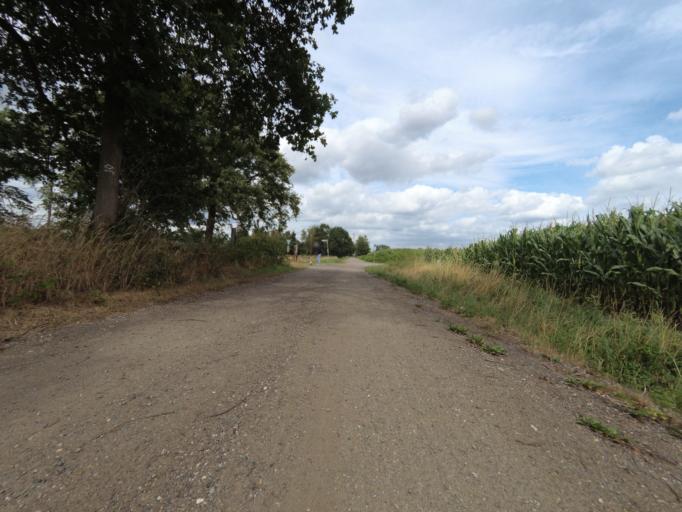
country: DE
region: North Rhine-Westphalia
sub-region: Regierungsbezirk Munster
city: Gronau
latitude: 52.1867
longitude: 6.9667
